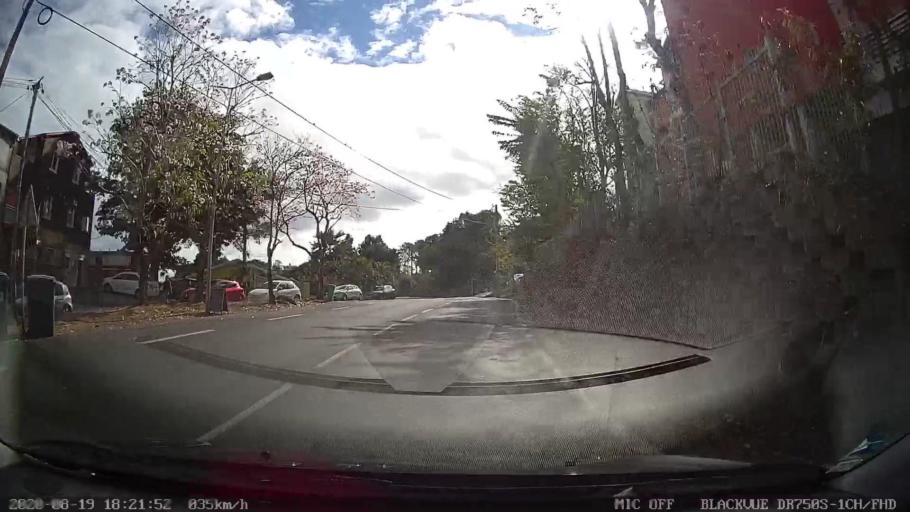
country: RE
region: Reunion
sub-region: Reunion
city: La Possession
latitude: -20.9567
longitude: 55.3367
